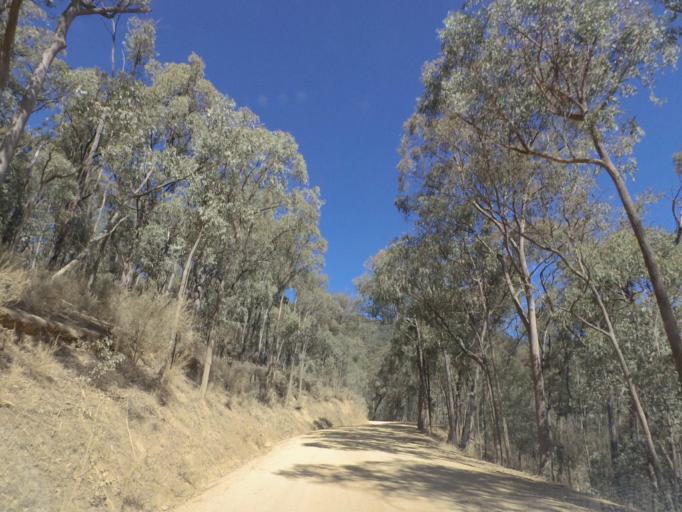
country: AU
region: Victoria
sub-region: Murrindindi
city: Alexandra
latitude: -37.3196
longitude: 145.8100
